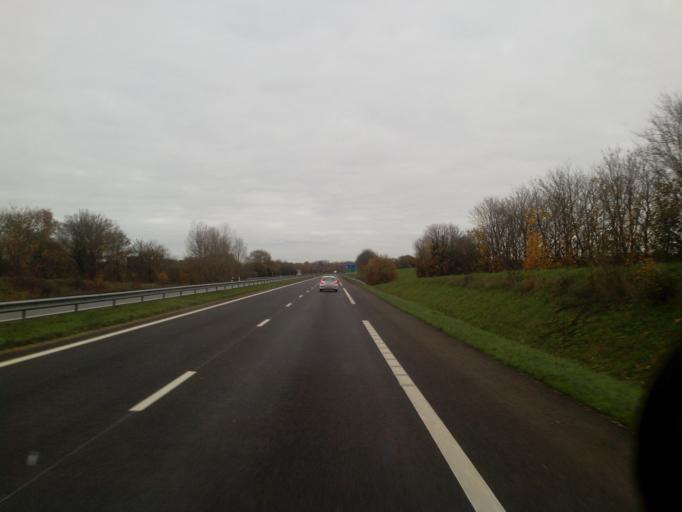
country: FR
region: Pays de la Loire
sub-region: Departement de Maine-et-Loire
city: Saint-Andre-de-la-Marche
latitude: 47.0906
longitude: -0.9952
